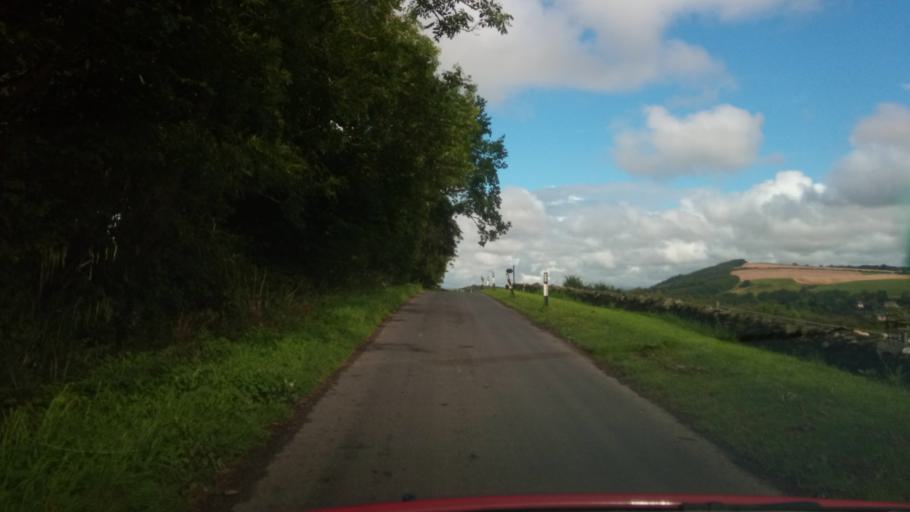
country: GB
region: Scotland
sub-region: The Scottish Borders
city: Earlston
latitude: 55.6305
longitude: -2.6846
